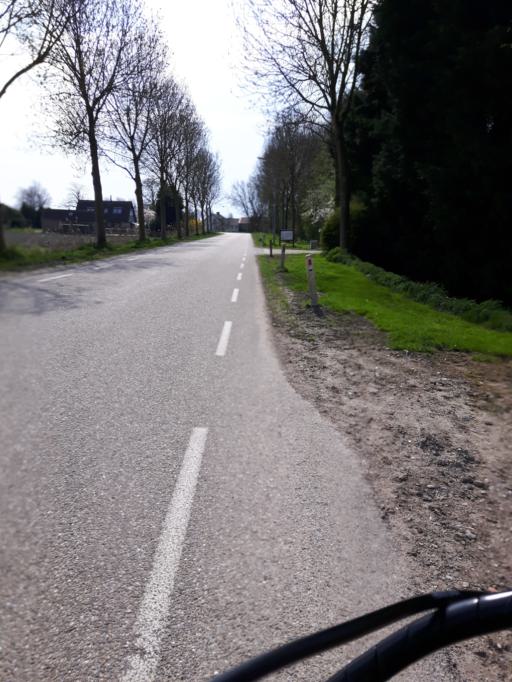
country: NL
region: Zeeland
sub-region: Gemeente Goes
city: Goes
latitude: 51.5047
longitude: 3.9492
